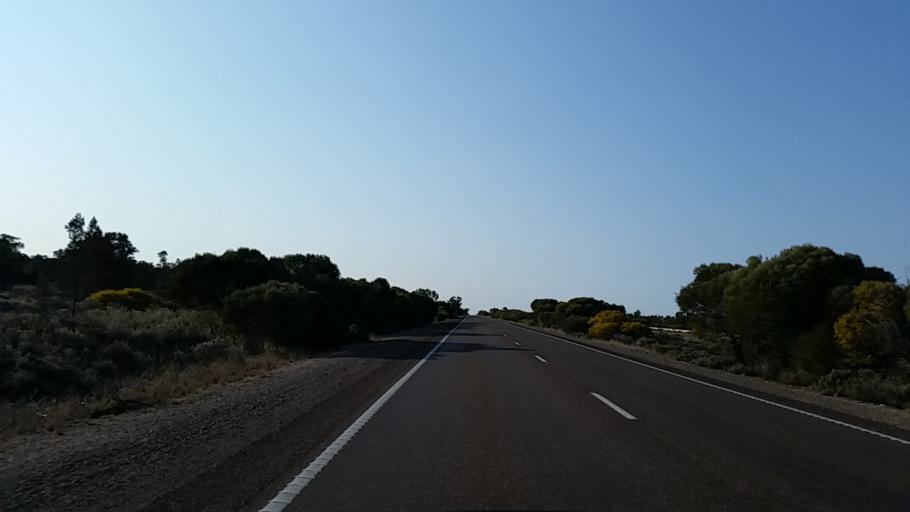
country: AU
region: South Australia
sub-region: Whyalla
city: Whyalla
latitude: -32.8141
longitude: 137.5423
